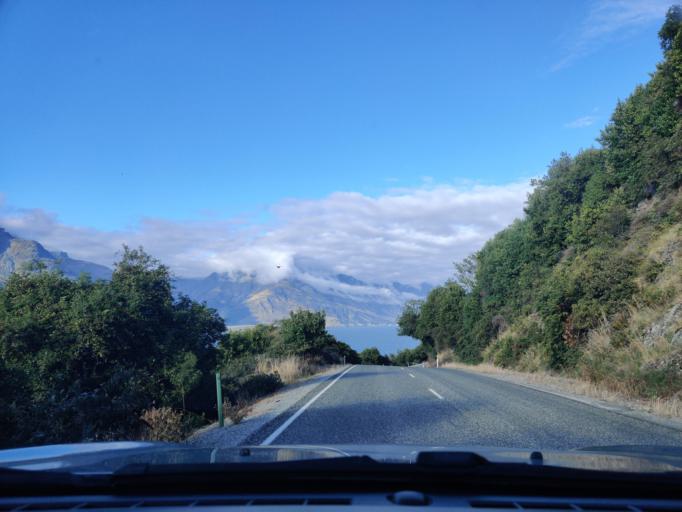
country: NZ
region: Otago
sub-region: Queenstown-Lakes District
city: Queenstown
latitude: -45.0548
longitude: 168.6150
